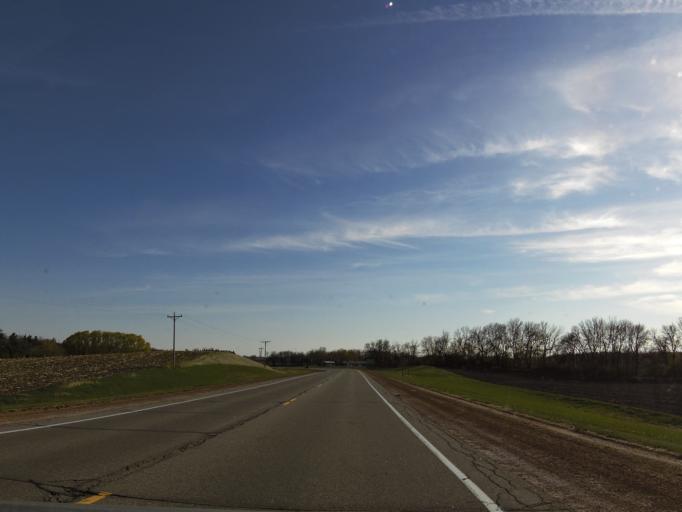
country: US
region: Minnesota
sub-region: Le Sueur County
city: New Prague
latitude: 44.5937
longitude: -93.5049
